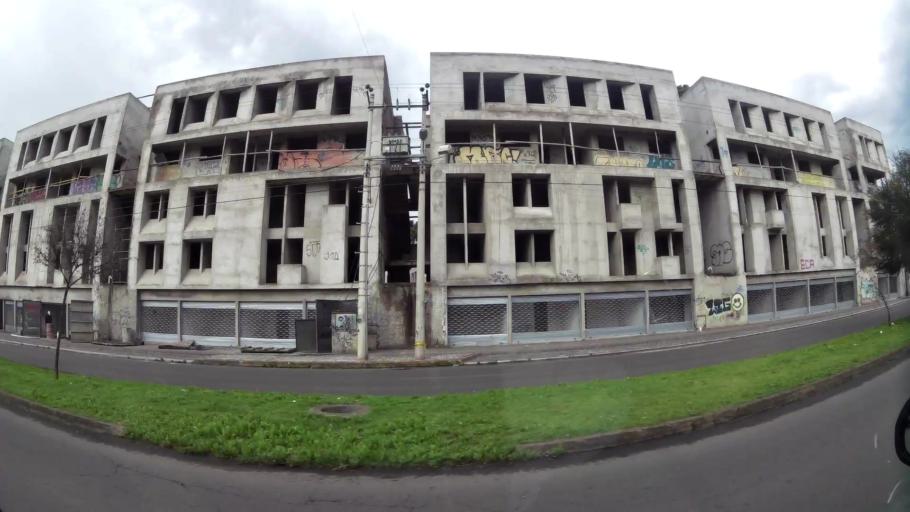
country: EC
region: Pichincha
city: Quito
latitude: -0.2908
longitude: -78.5507
